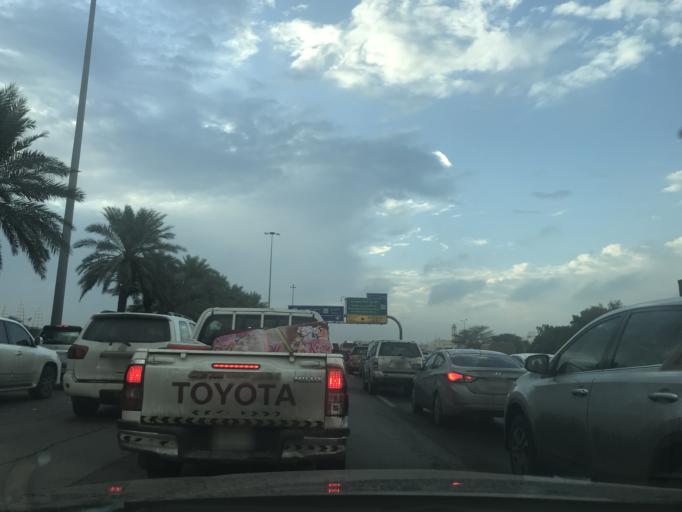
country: SA
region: Ar Riyad
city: Riyadh
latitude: 24.7850
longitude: 46.7260
